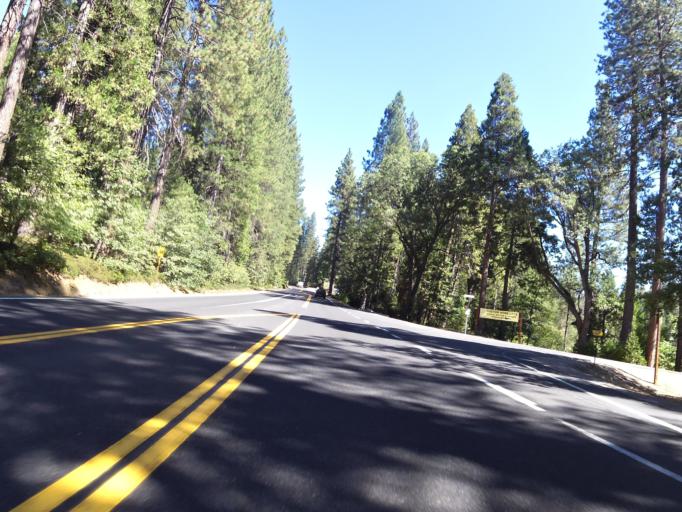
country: US
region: California
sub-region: Calaveras County
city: Arnold
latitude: 38.2208
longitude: -120.3692
